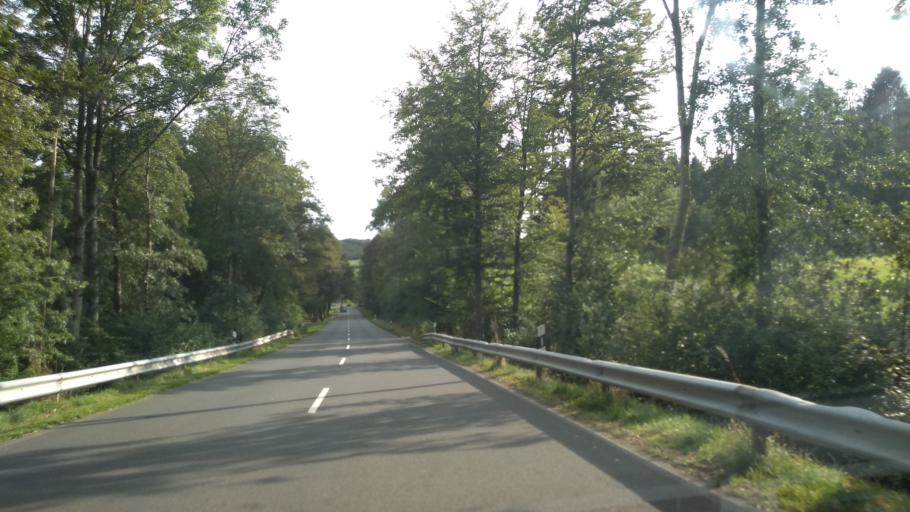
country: DE
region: North Rhine-Westphalia
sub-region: Regierungsbezirk Koln
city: Much
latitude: 50.9176
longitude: 7.4049
